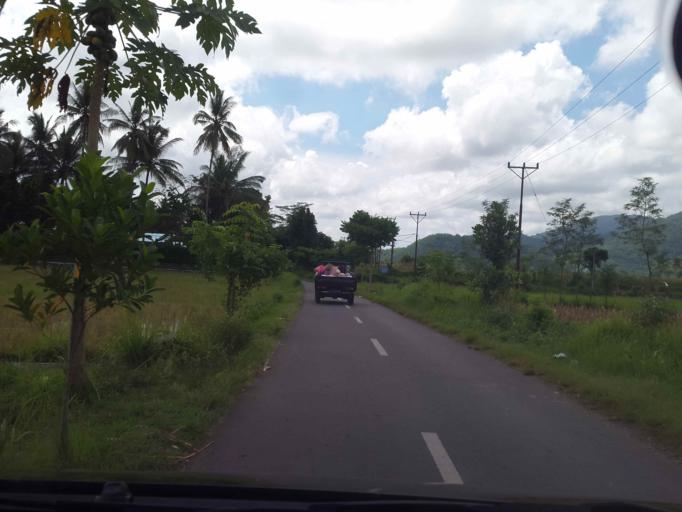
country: ID
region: West Nusa Tenggara
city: Ranggagata
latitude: -8.6943
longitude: 116.1440
